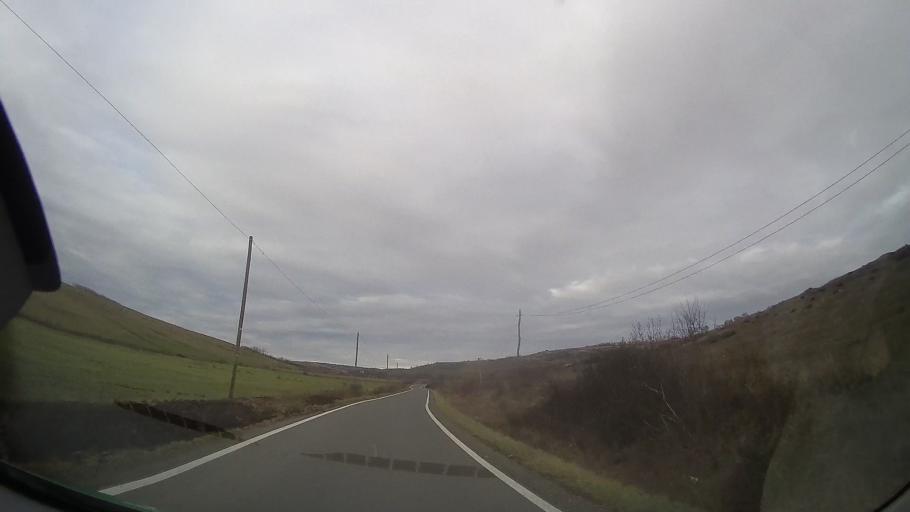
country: RO
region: Mures
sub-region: Comuna Cozma
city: Cozma
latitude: 46.7973
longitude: 24.5397
